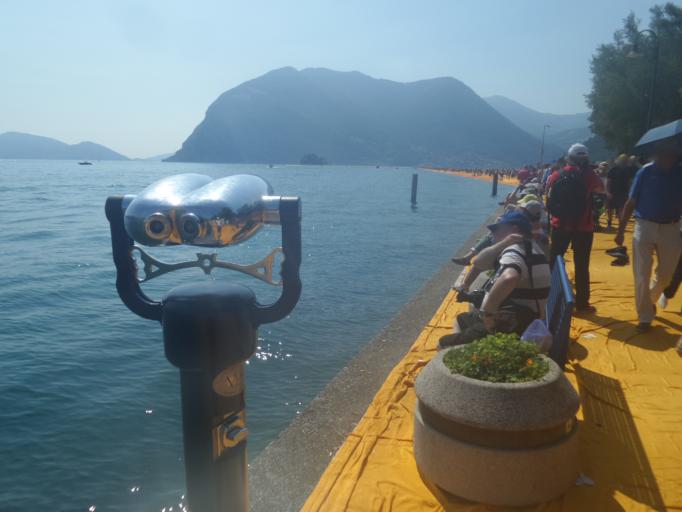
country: IT
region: Lombardy
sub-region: Provincia di Brescia
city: Sulzano
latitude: 45.6940
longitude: 10.0867
